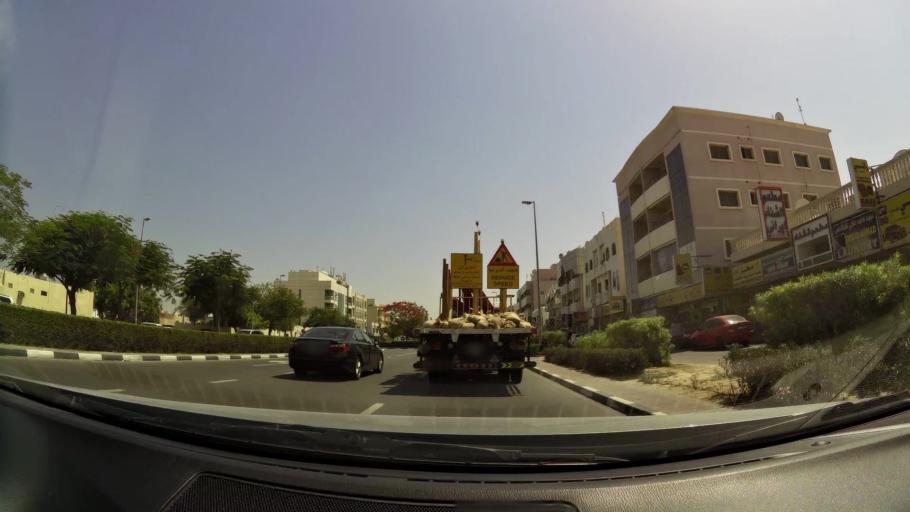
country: AE
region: Ash Shariqah
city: Sharjah
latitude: 25.2249
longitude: 55.2723
